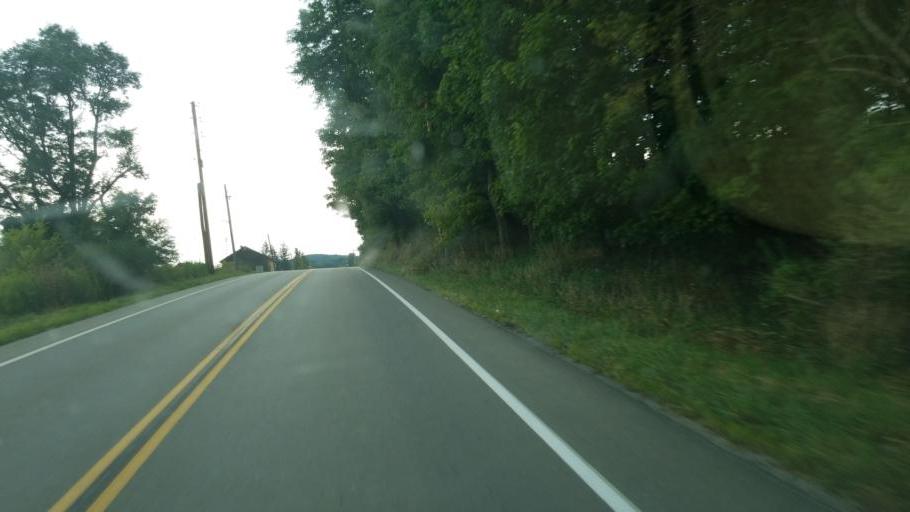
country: US
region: Pennsylvania
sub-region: Clarion County
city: Knox
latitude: 41.1955
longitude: -79.6657
